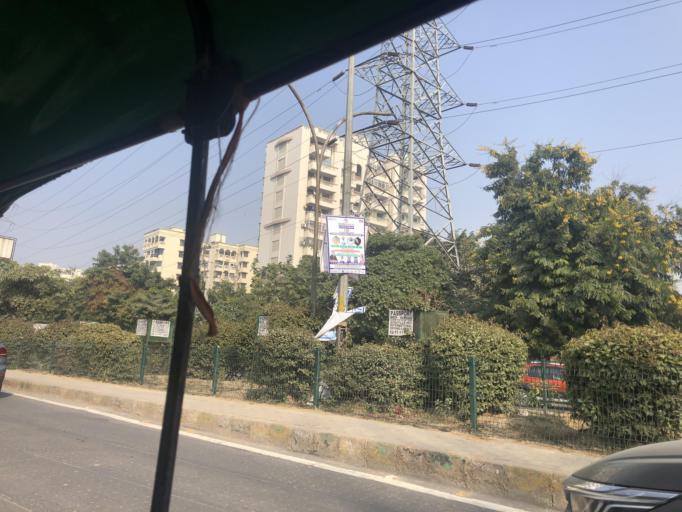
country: IN
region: Haryana
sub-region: Gurgaon
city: Gurgaon
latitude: 28.4475
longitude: 77.0792
